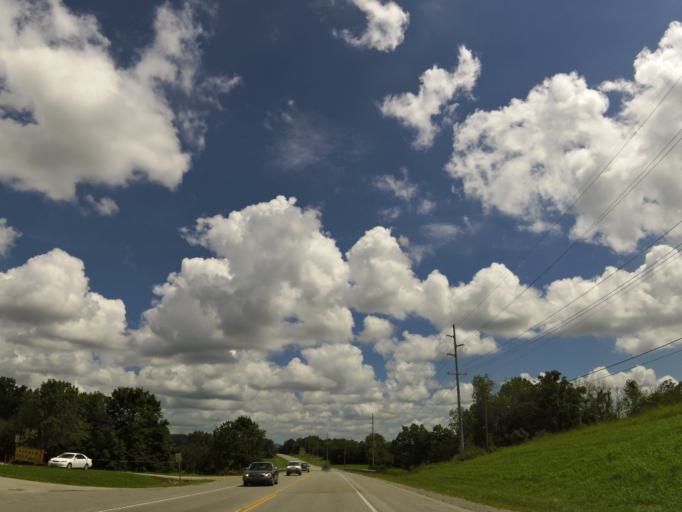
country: US
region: Kentucky
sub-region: Bell County
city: Middlesboro
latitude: 36.4955
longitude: -83.8127
